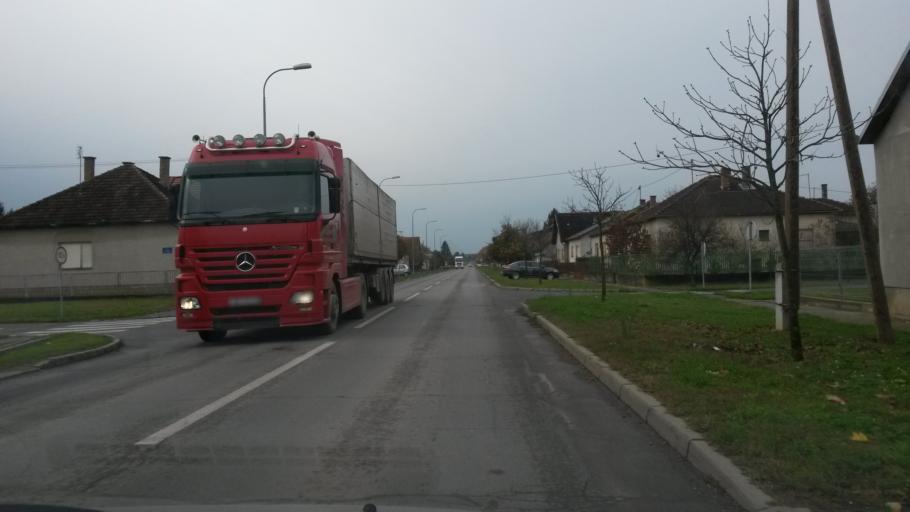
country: HR
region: Osjecko-Baranjska
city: Beli Manastir
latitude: 45.7667
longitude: 18.6132
